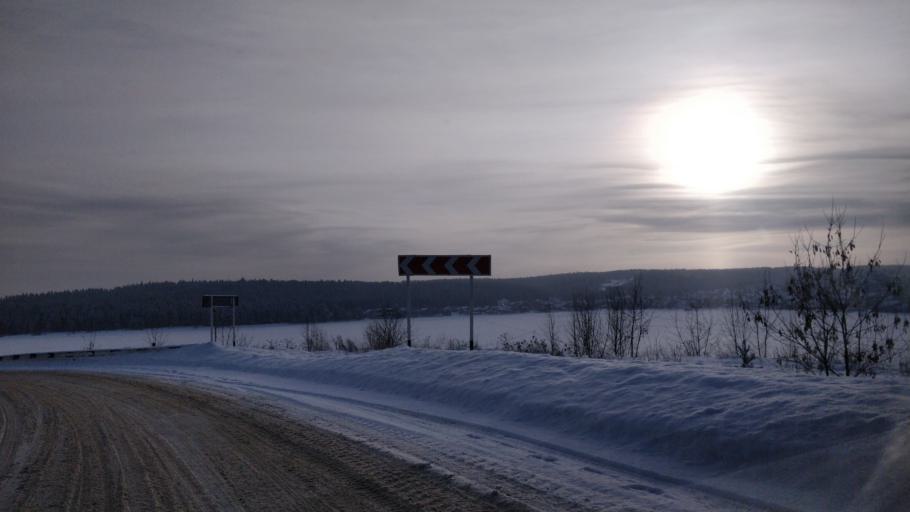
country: RU
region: Perm
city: Polazna
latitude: 58.3062
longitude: 56.4245
